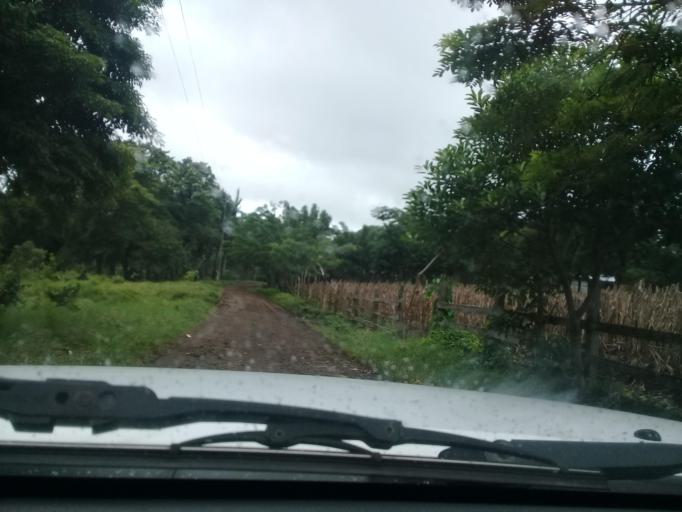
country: MX
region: Veracruz
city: Santiago Tuxtla
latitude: 18.4373
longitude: -95.2971
